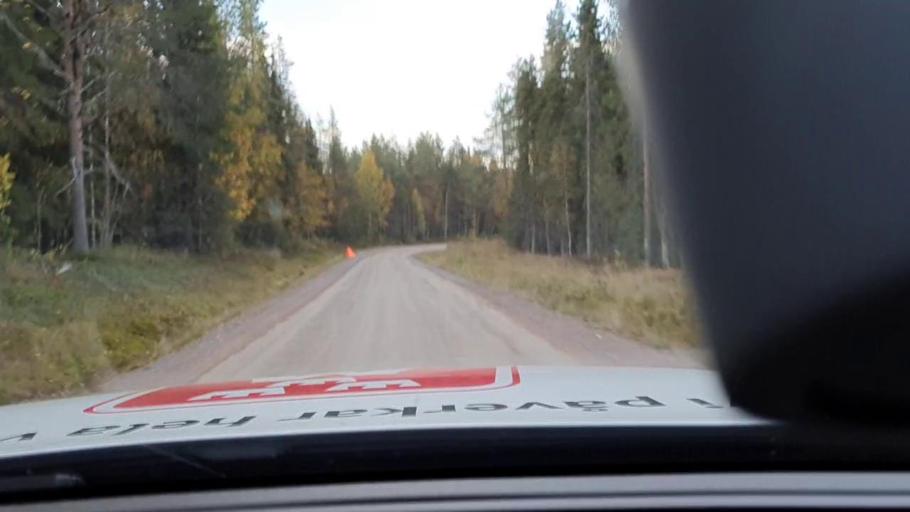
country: SE
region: Norrbotten
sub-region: Overkalix Kommun
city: OEverkalix
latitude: 66.3210
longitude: 22.6928
